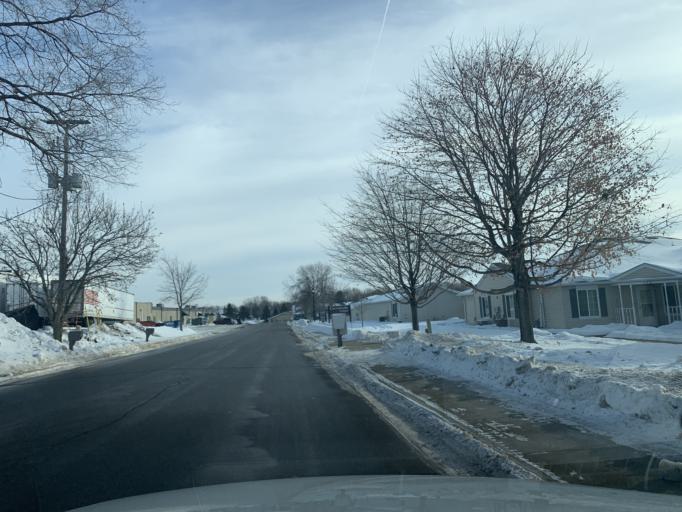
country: US
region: Minnesota
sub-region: Wright County
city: Saint Michael
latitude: 45.2089
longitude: -93.6576
